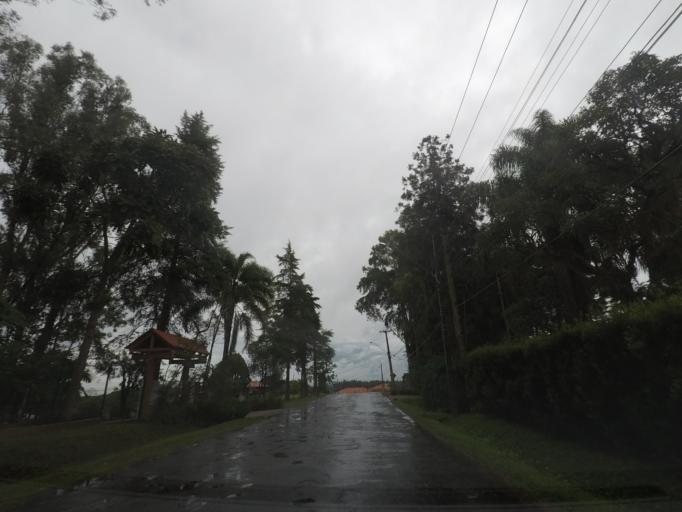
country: BR
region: Parana
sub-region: Campo Largo
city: Campo Largo
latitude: -25.4581
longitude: -49.4299
